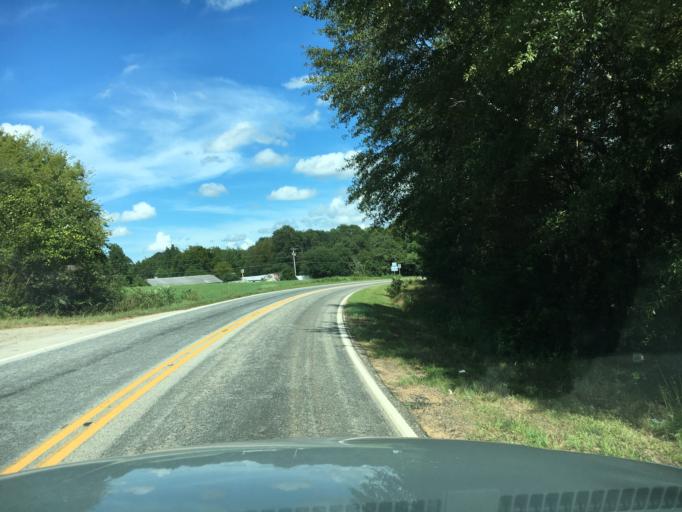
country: US
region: South Carolina
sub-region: Greenwood County
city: Ware Shoals
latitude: 34.4214
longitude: -82.2827
